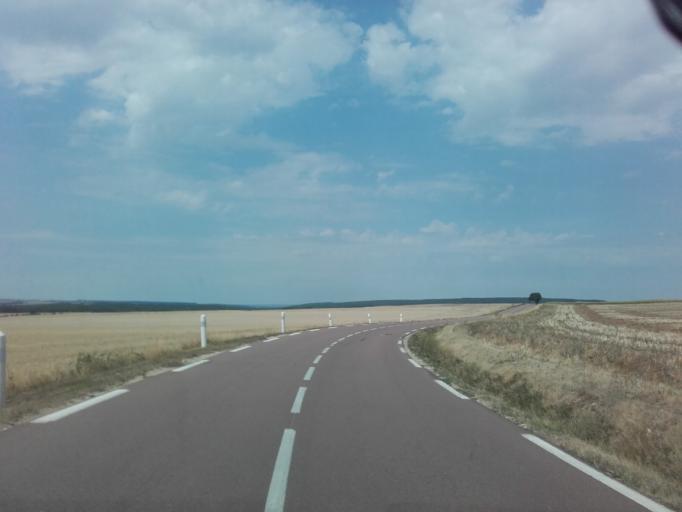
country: FR
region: Bourgogne
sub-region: Departement de l'Yonne
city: Joux-la-Ville
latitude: 47.7122
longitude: 3.8528
